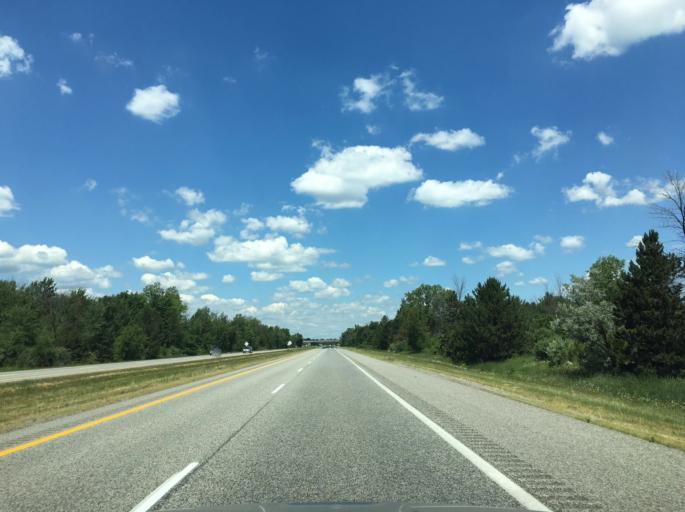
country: US
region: Michigan
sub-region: Midland County
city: Midland
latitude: 43.6339
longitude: -84.1822
